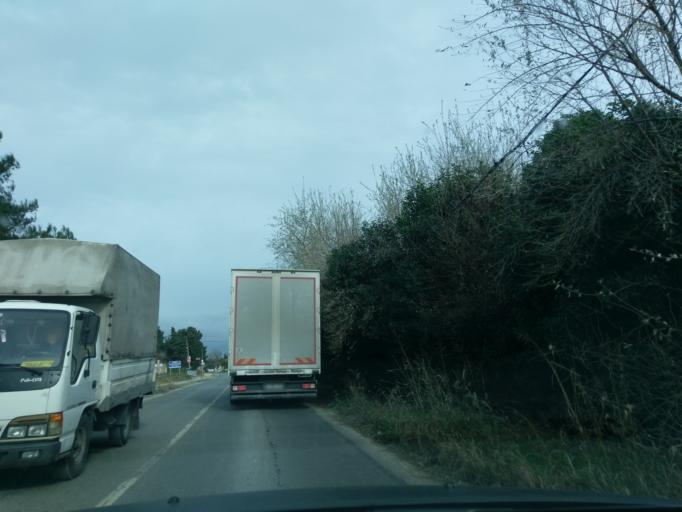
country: TR
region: Istanbul
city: Selimpasa
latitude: 41.0673
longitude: 28.3702
